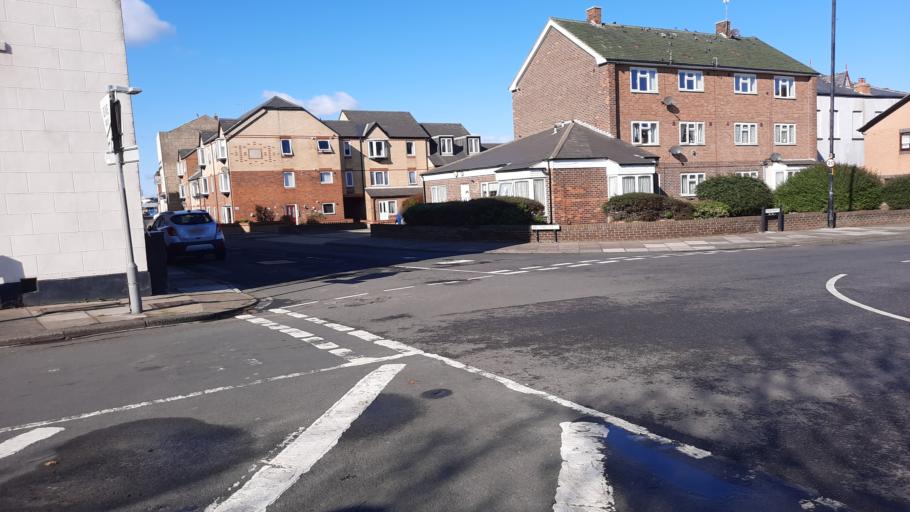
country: GB
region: England
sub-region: Hartlepool
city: Hartlepool
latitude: 54.6955
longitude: -1.1848
